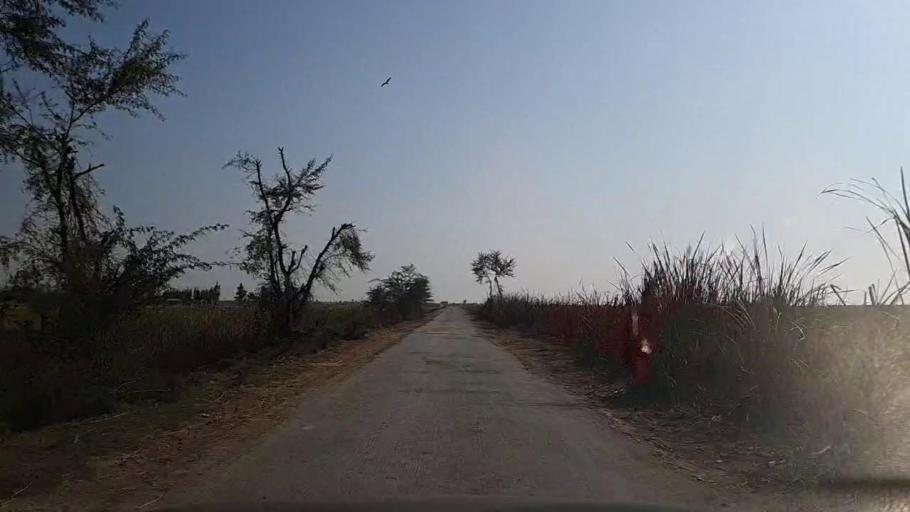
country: PK
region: Sindh
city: Sanghar
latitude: 26.0052
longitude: 69.0225
